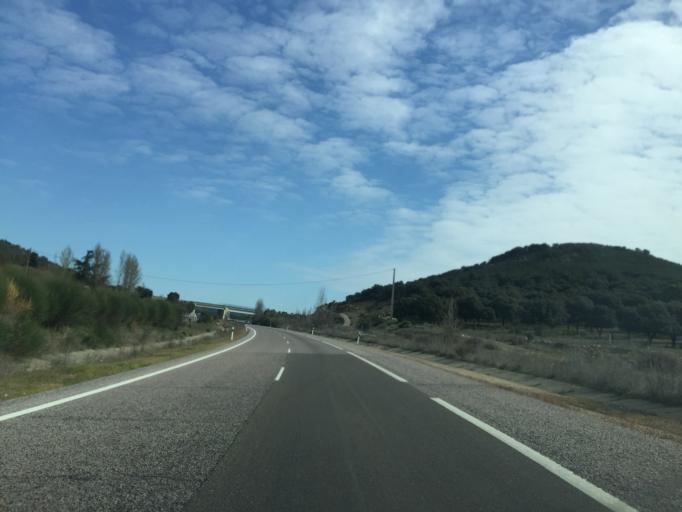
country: ES
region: Castille and Leon
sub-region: Provincia de Salamanca
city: Ciudad Rodrigo
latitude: 40.6270
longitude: -6.4980
